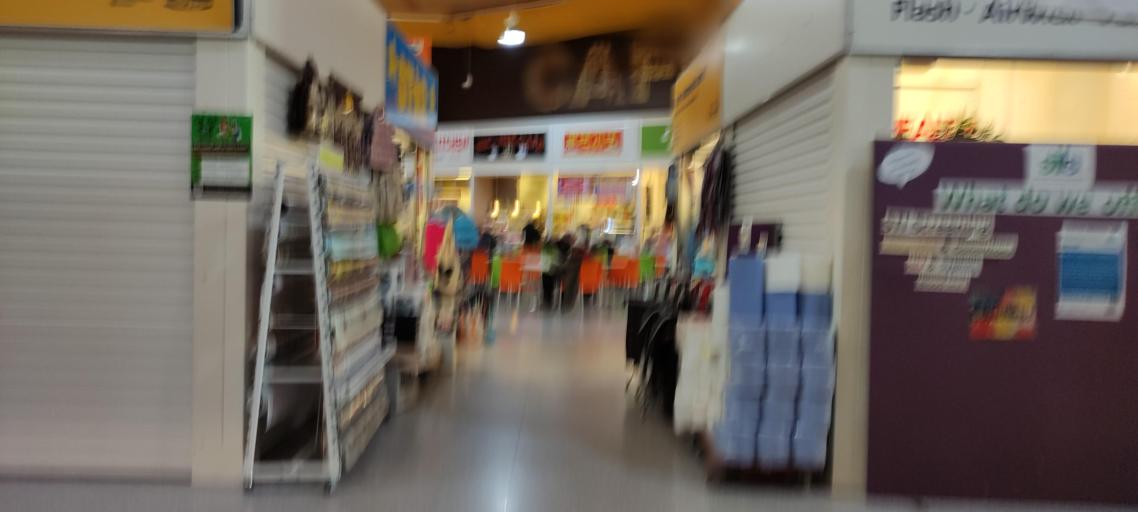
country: GB
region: England
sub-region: Sheffield
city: Sheffield
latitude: 53.3755
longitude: -1.4727
